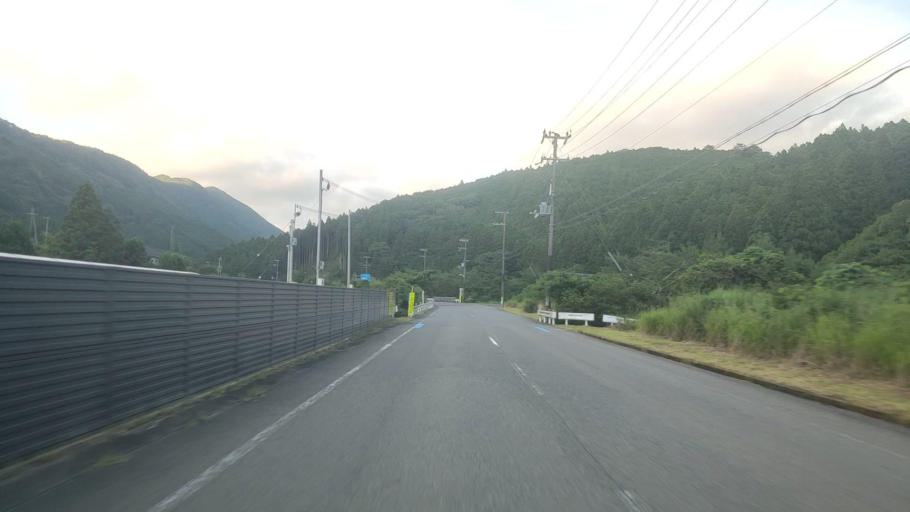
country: JP
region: Wakayama
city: Tanabe
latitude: 33.8215
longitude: 135.6297
